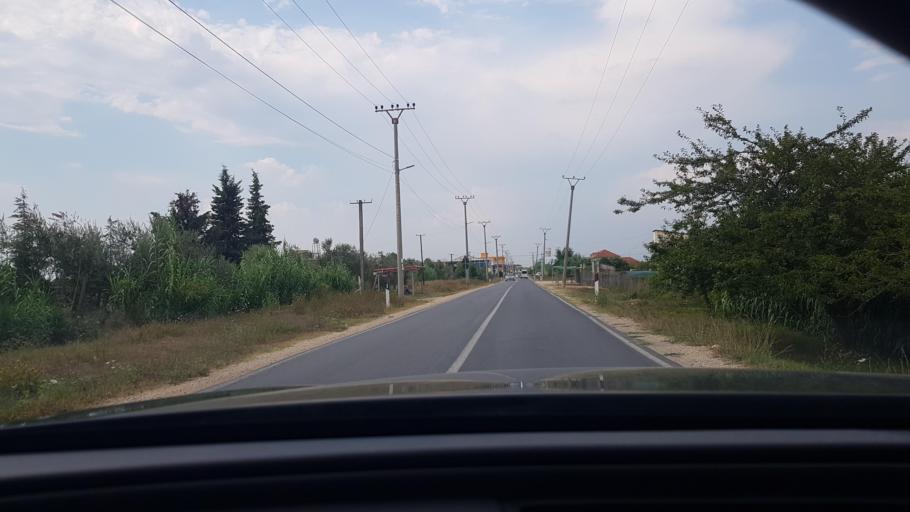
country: AL
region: Durres
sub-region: Rrethi i Durresit
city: Katundi i Ri
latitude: 41.4223
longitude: 19.5486
